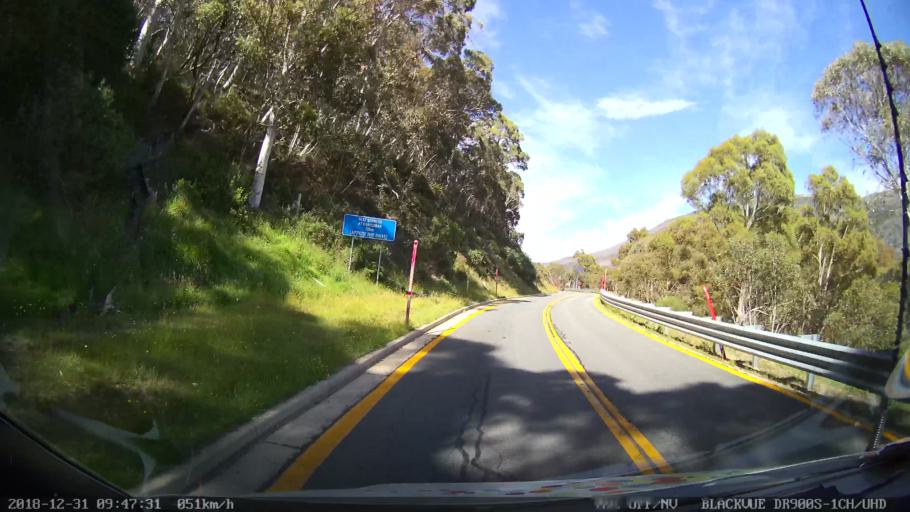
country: AU
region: New South Wales
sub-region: Snowy River
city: Jindabyne
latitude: -36.5088
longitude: 148.3010
